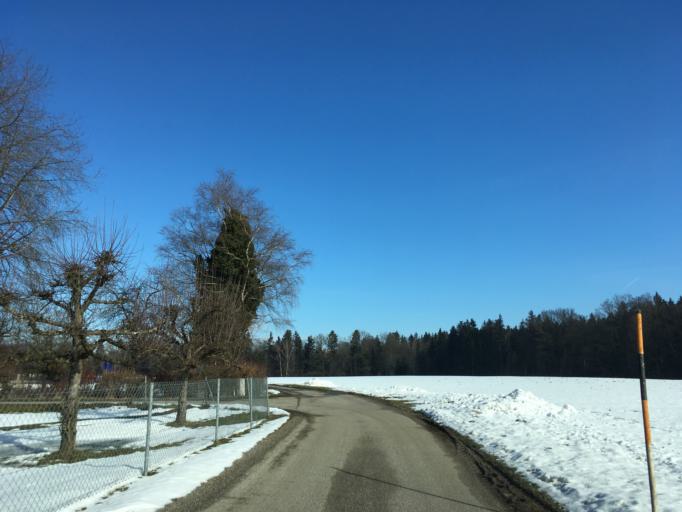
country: DE
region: Bavaria
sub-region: Upper Bavaria
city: Schechen
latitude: 47.9135
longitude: 12.1507
